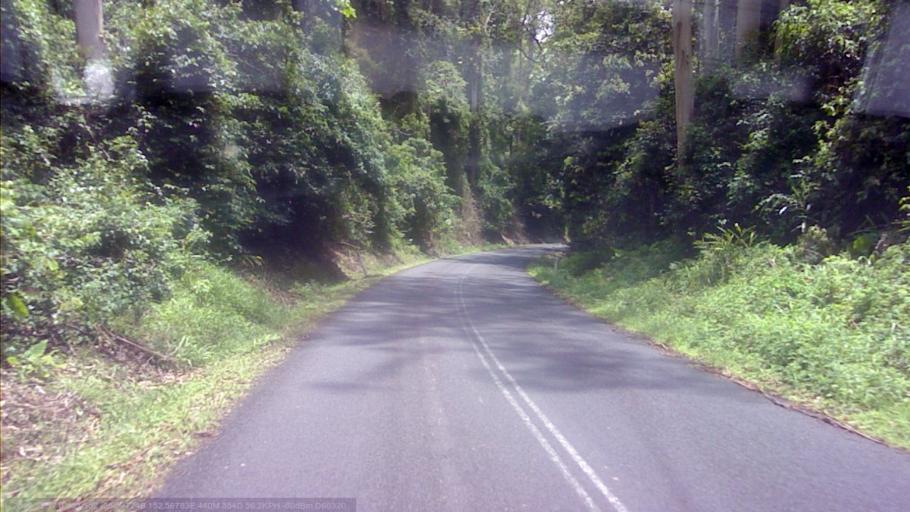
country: AU
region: New South Wales
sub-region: Kyogle
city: Kyogle
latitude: -28.5072
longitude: 152.5678
